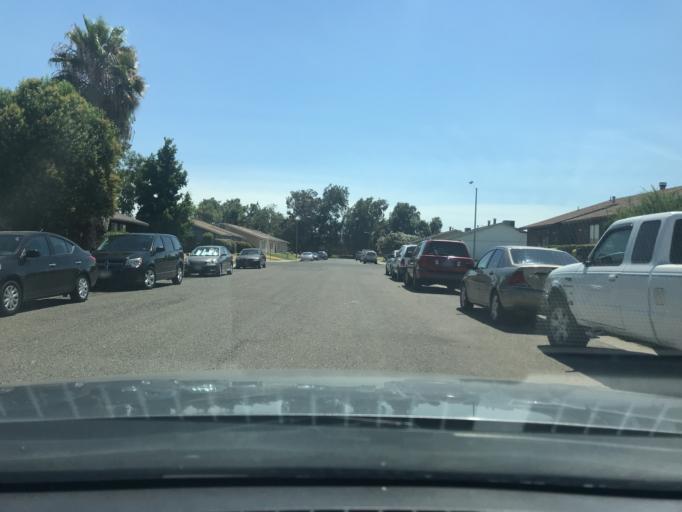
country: US
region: California
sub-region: Merced County
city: Merced
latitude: 37.3206
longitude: -120.4937
